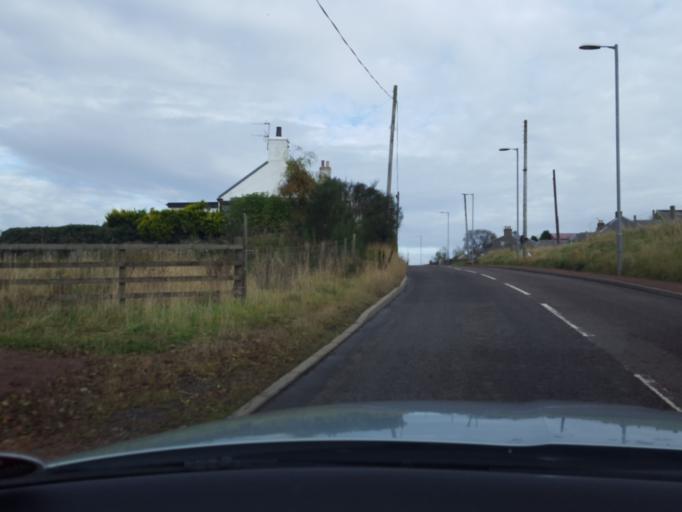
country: GB
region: Scotland
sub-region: South Lanarkshire
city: Biggar
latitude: 55.6759
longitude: -3.4934
